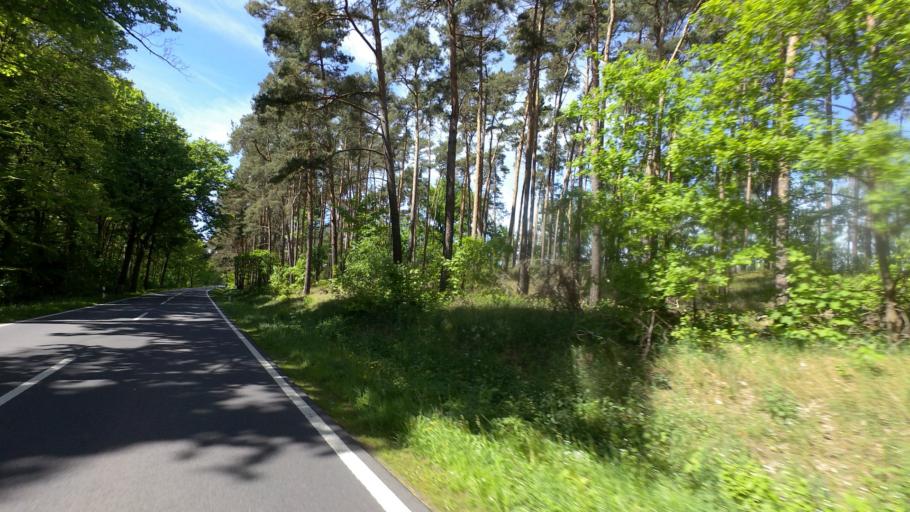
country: DE
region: Brandenburg
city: Baruth
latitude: 52.0658
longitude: 13.4756
